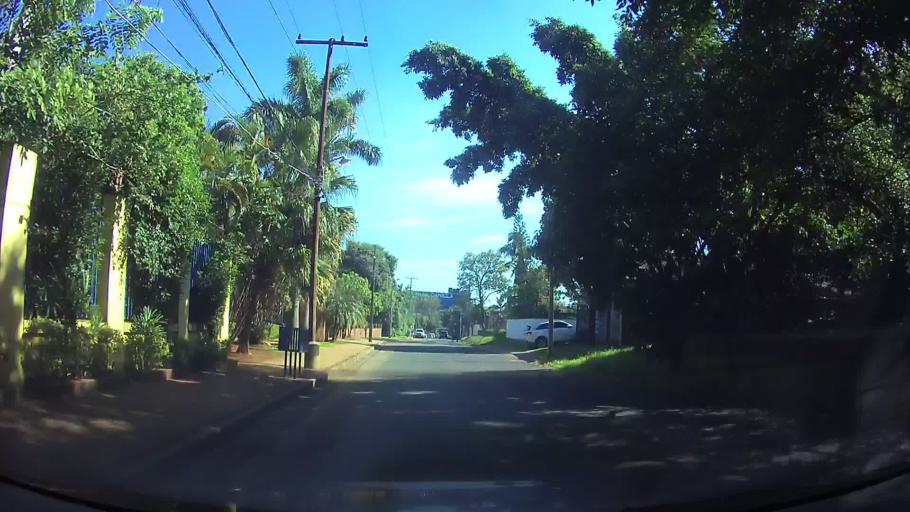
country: PY
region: Central
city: Fernando de la Mora
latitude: -25.2658
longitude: -57.5143
